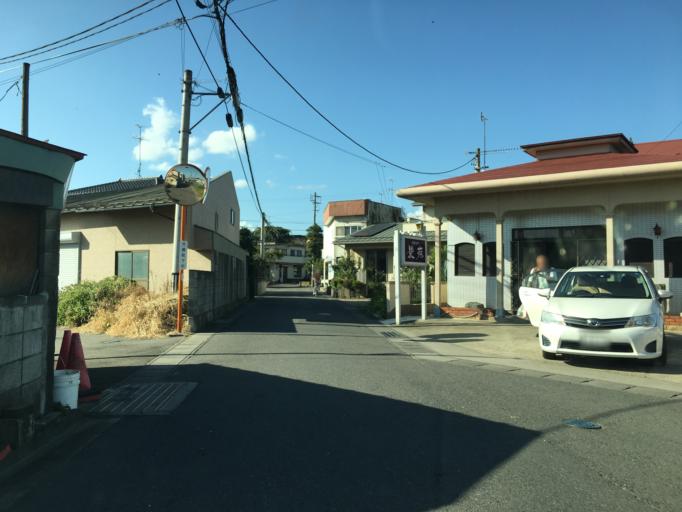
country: JP
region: Fukushima
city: Koriyama
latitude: 37.3880
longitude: 140.3233
